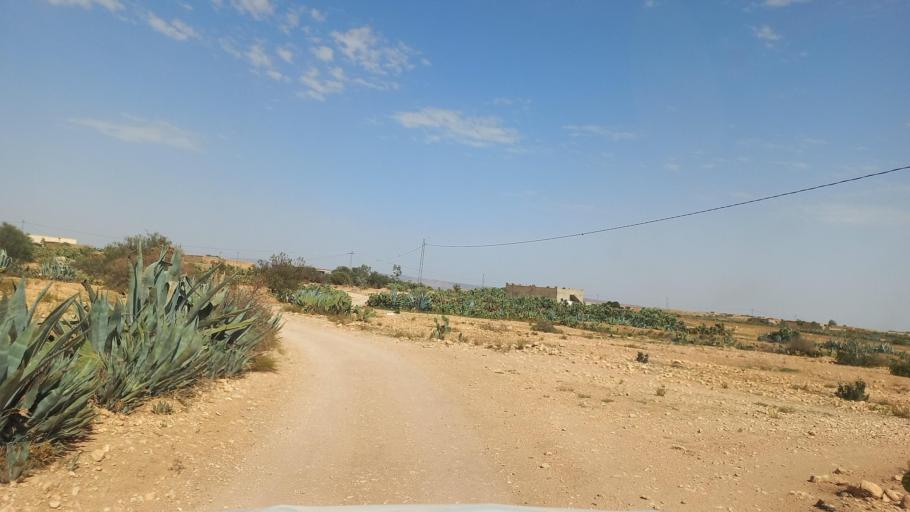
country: TN
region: Al Qasrayn
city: Kasserine
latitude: 35.2794
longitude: 8.9554
